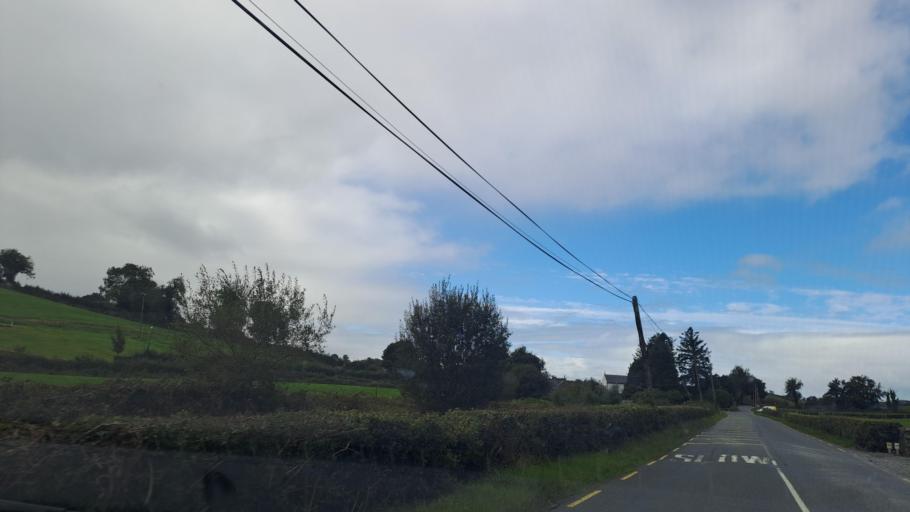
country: IE
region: Ulster
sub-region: An Cabhan
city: Kingscourt
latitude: 53.9973
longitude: -6.8329
